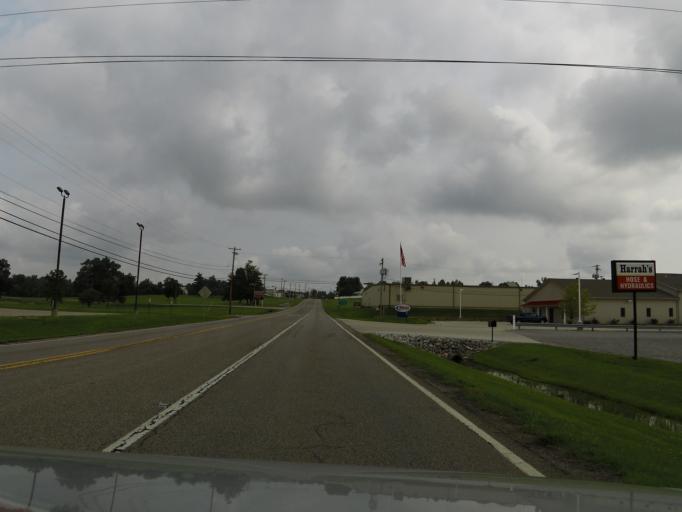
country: US
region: Kentucky
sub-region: Hopkins County
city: Madisonville
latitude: 37.3776
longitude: -87.4899
